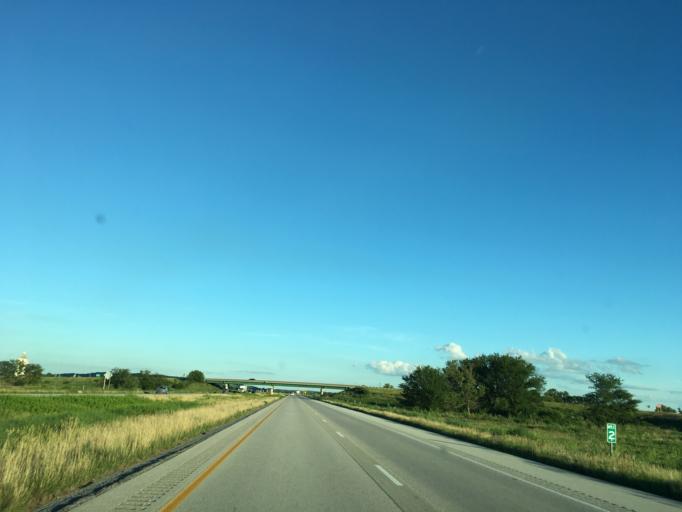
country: US
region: Iowa
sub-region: Fremont County
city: Hamburg
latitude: 40.6035
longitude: -95.6804
